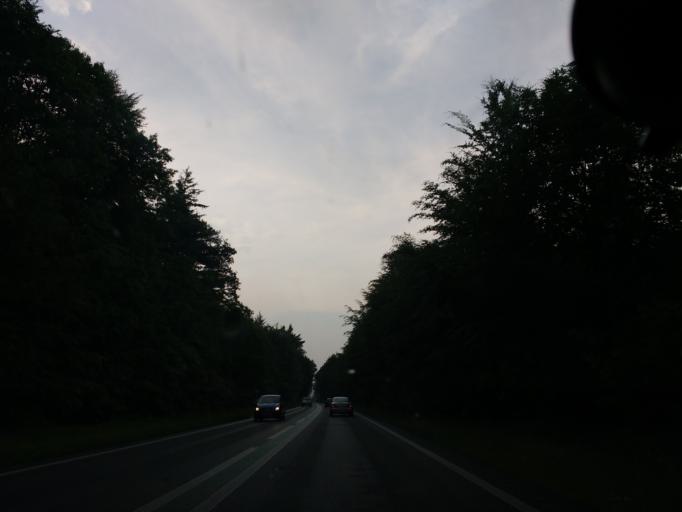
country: NL
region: Drenthe
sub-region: Gemeente Borger-Odoorn
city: Borger
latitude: 52.8698
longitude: 6.8339
